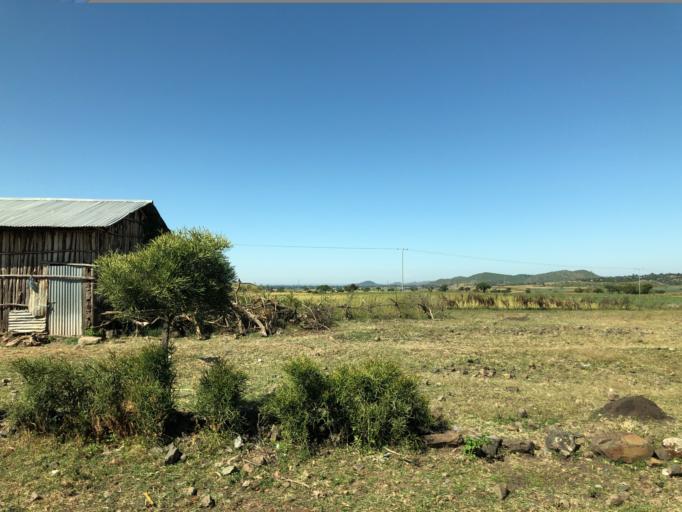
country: ET
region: Amhara
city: Adis Zemen
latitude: 12.1906
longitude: 37.6734
